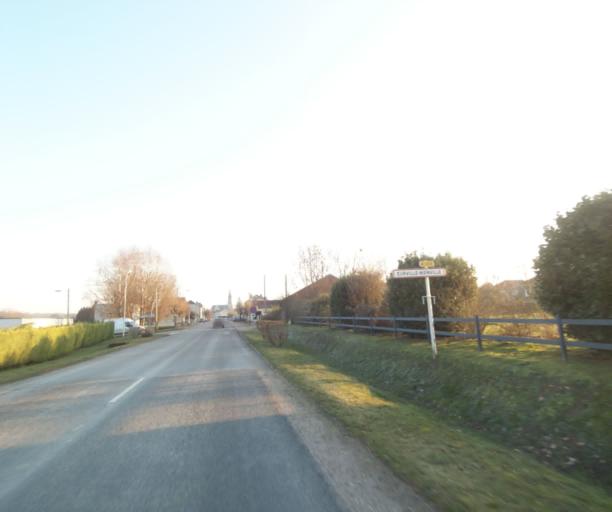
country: FR
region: Champagne-Ardenne
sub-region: Departement de la Haute-Marne
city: Bienville
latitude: 48.5897
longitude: 5.0338
